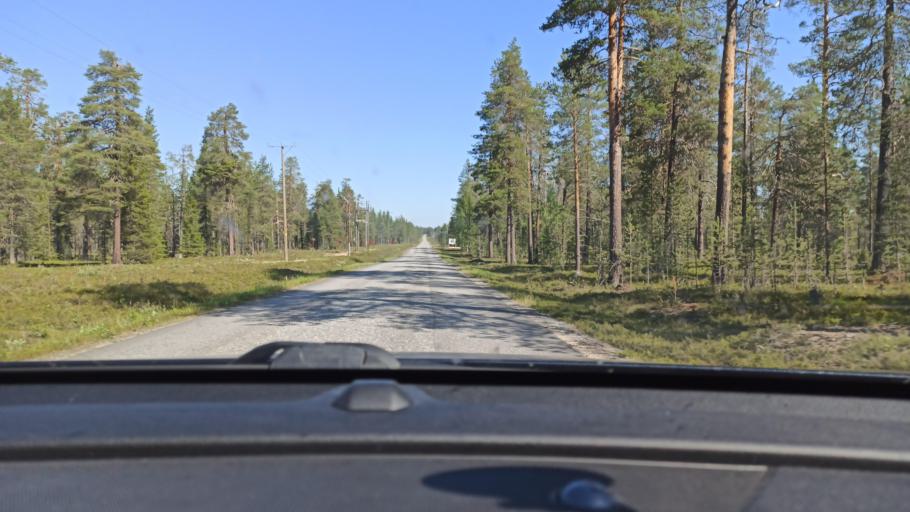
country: FI
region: Lapland
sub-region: Tunturi-Lappi
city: Kolari
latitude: 67.6439
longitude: 24.1592
